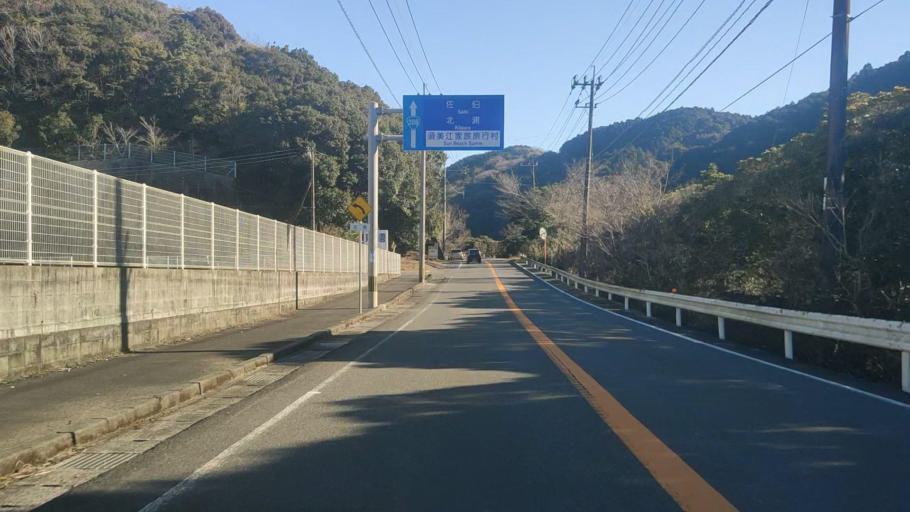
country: JP
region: Miyazaki
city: Nobeoka
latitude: 32.6187
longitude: 131.7026
